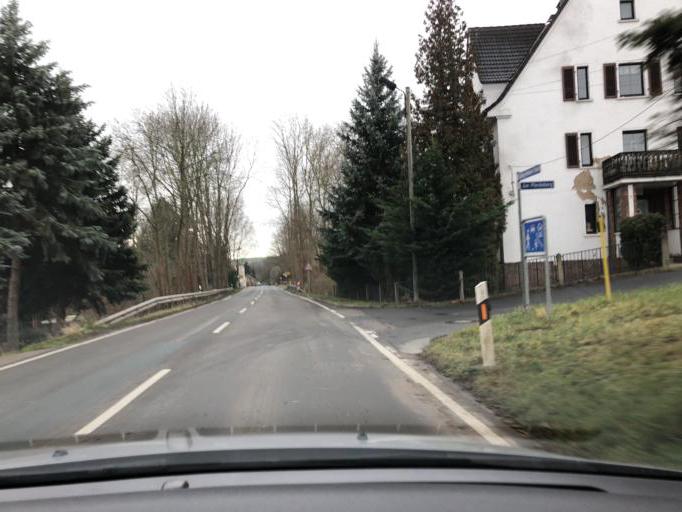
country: DE
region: Saxony
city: Ebersbach
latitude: 51.1014
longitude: 13.1314
